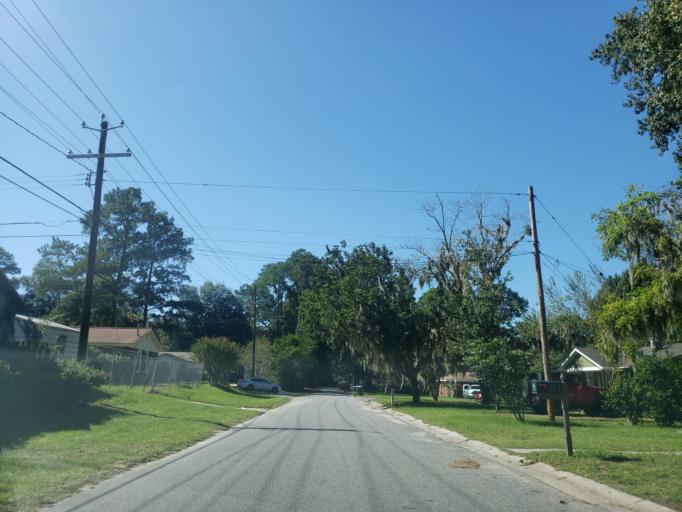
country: US
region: Georgia
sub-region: Chatham County
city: Thunderbolt
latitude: 32.0372
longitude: -81.0719
